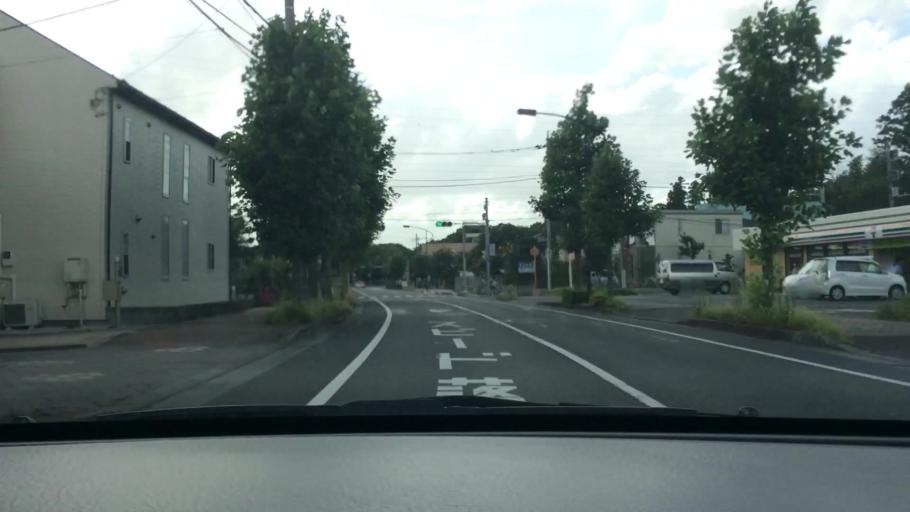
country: JP
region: Chiba
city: Nagareyama
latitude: 35.8991
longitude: 139.9280
